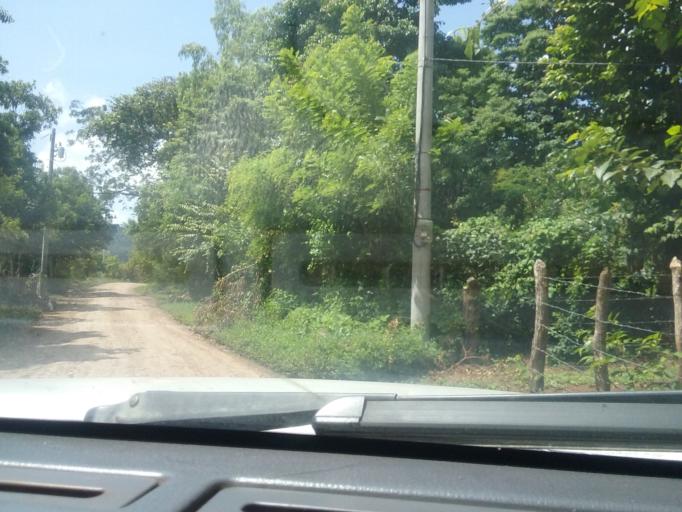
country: NI
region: Matagalpa
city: Terrabona
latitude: 12.7016
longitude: -85.9509
